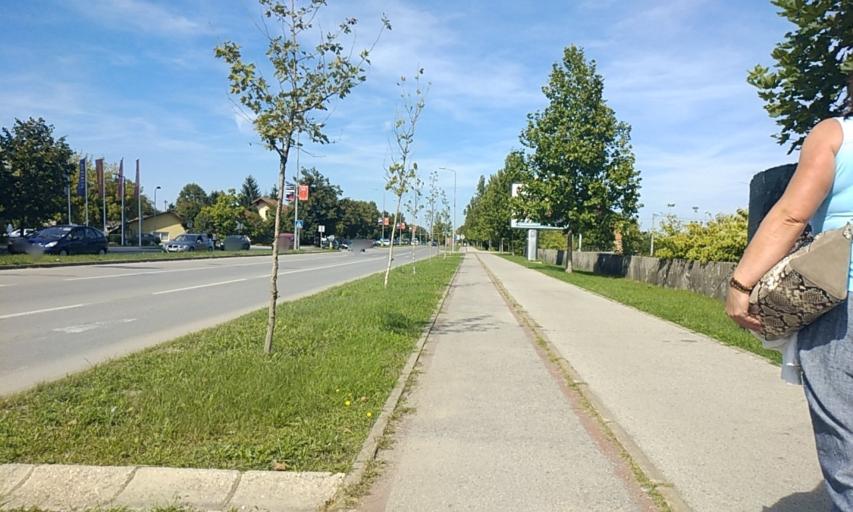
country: BA
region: Republika Srpska
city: Banja Luka
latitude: 44.7813
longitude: 17.2063
